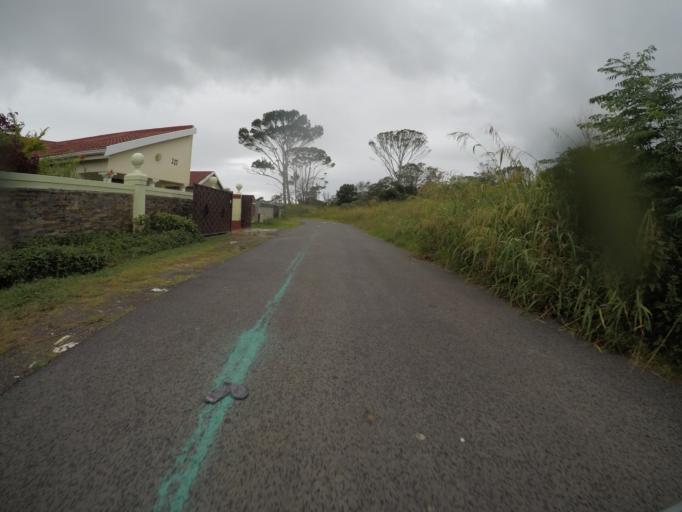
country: ZA
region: Eastern Cape
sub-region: Buffalo City Metropolitan Municipality
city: East London
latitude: -32.9947
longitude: 27.8377
